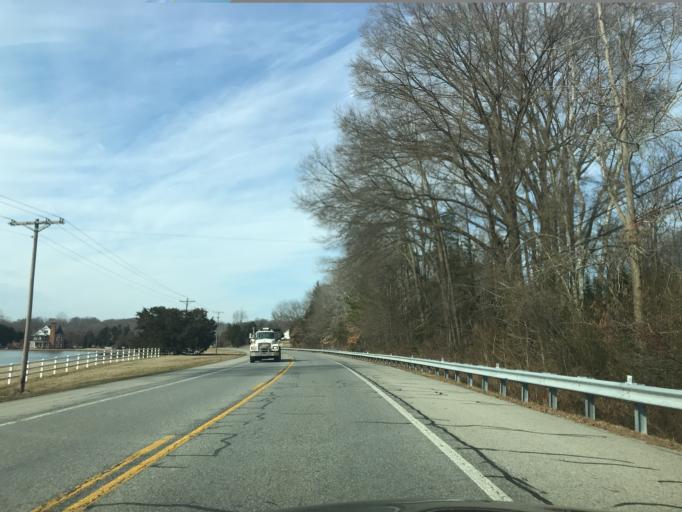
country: US
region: Maryland
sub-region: Charles County
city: La Plata
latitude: 38.5224
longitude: -77.0055
